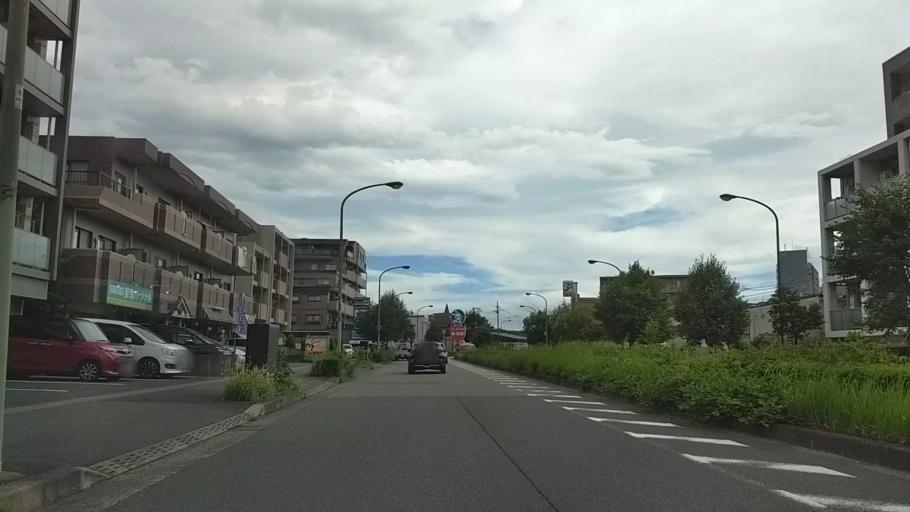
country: JP
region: Tokyo
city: Hachioji
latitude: 35.6362
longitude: 139.3302
